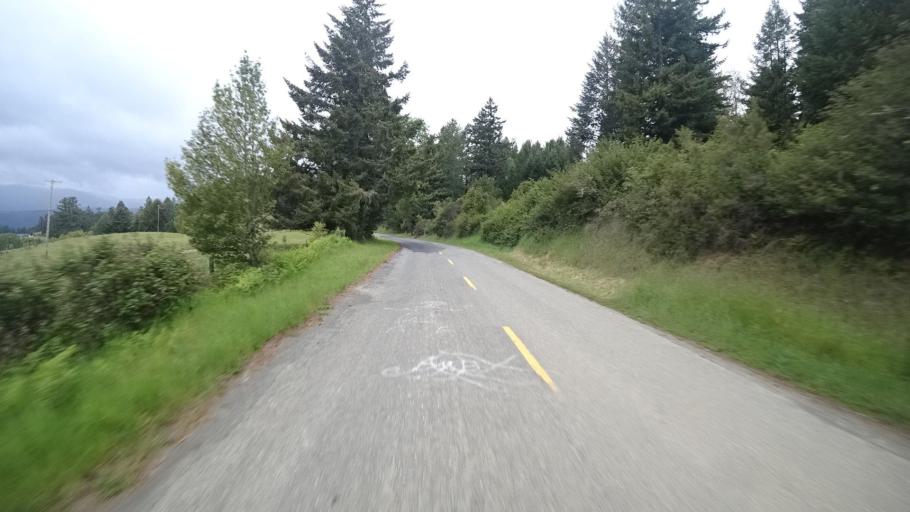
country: US
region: California
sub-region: Humboldt County
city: Redway
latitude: 40.2893
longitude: -123.8036
